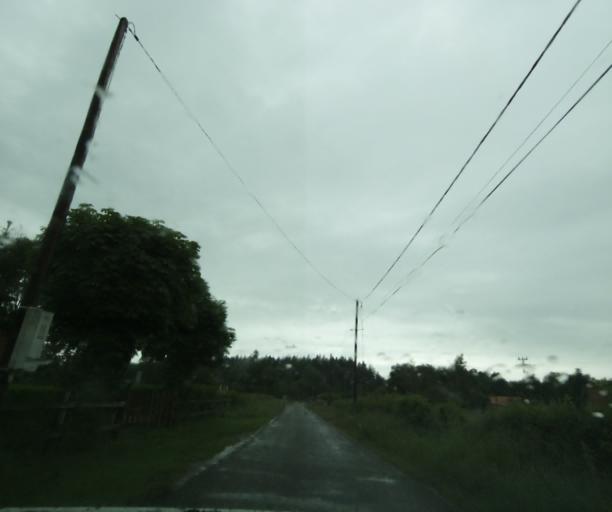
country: FR
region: Bourgogne
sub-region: Departement de Saone-et-Loire
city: Ciry-le-Noble
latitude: 46.5355
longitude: 4.3020
